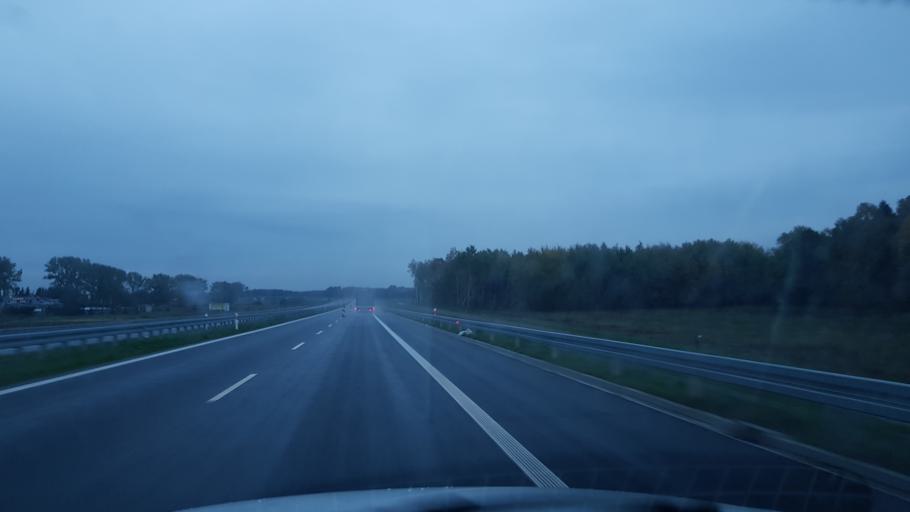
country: PL
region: West Pomeranian Voivodeship
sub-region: Powiat gryficki
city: Ploty
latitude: 53.8487
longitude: 15.3253
